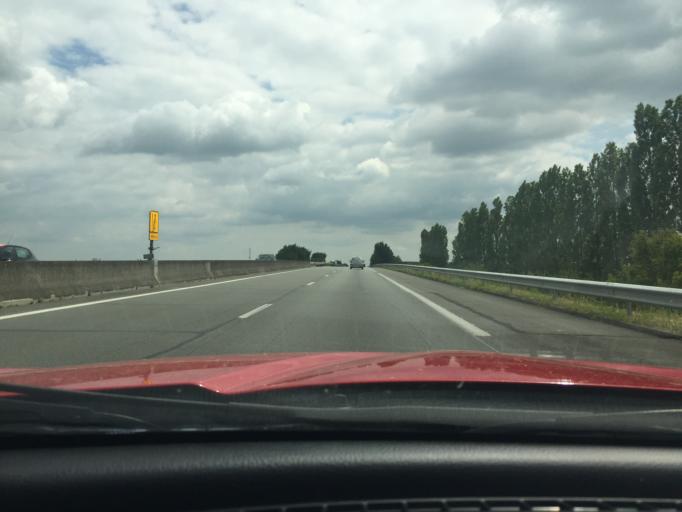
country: FR
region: Picardie
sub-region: Departement de l'Aisne
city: Aulnois-sous-Laon
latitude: 49.6134
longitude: 3.6470
